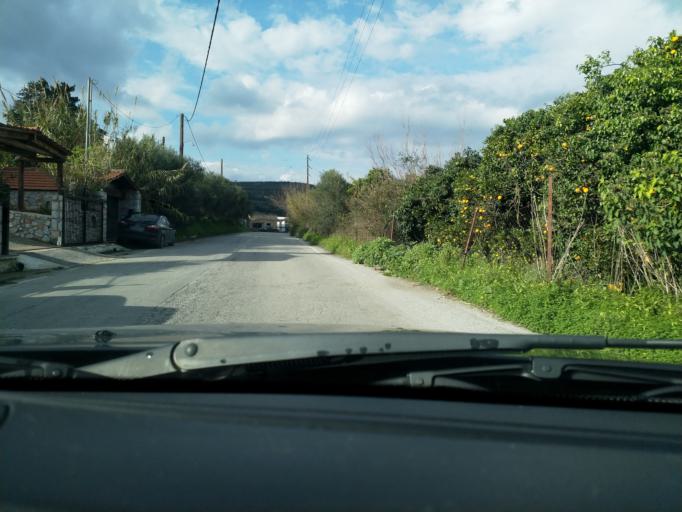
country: GR
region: Crete
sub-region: Nomos Chanias
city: Gerani
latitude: 35.5017
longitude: 23.8973
